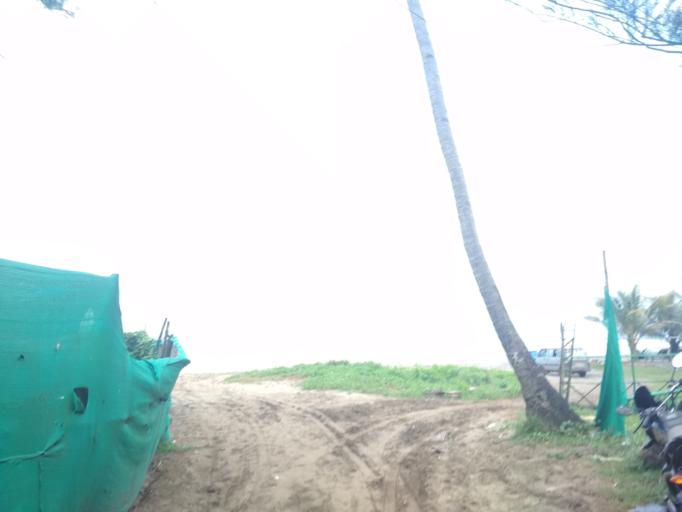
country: IN
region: Goa
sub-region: North Goa
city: Arambol
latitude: 15.6877
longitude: 73.7036
